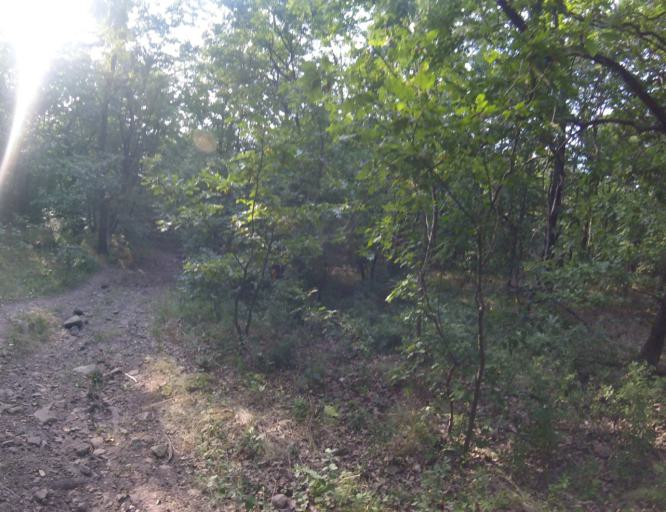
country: HU
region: Pest
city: Nagykovacsi
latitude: 47.6779
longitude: 19.0149
